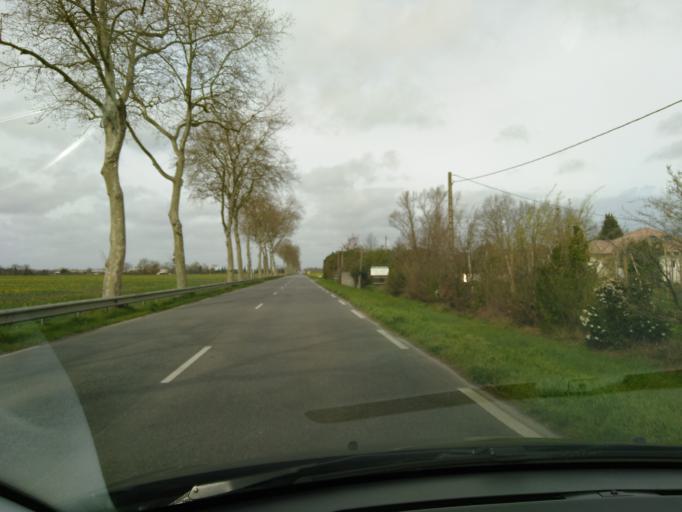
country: FR
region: Midi-Pyrenees
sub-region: Departement de la Haute-Garonne
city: Seilh
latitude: 43.7113
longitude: 1.3384
